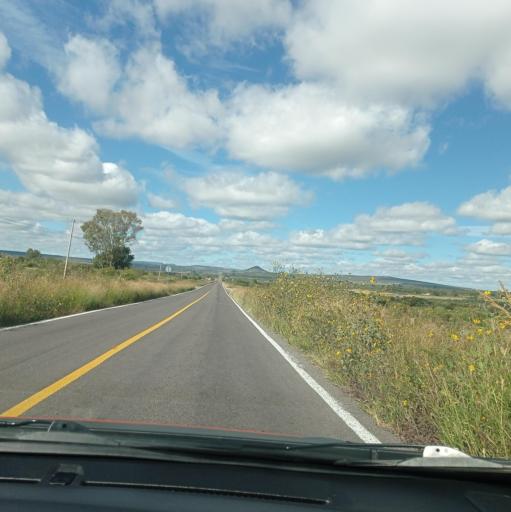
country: MX
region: Jalisco
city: San Diego de Alejandria
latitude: 21.0074
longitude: -102.0200
